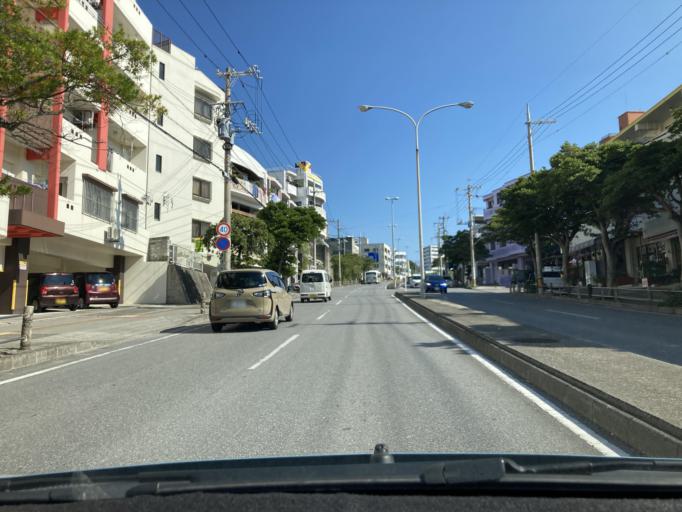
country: JP
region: Okinawa
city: Naha-shi
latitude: 26.2048
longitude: 127.7040
